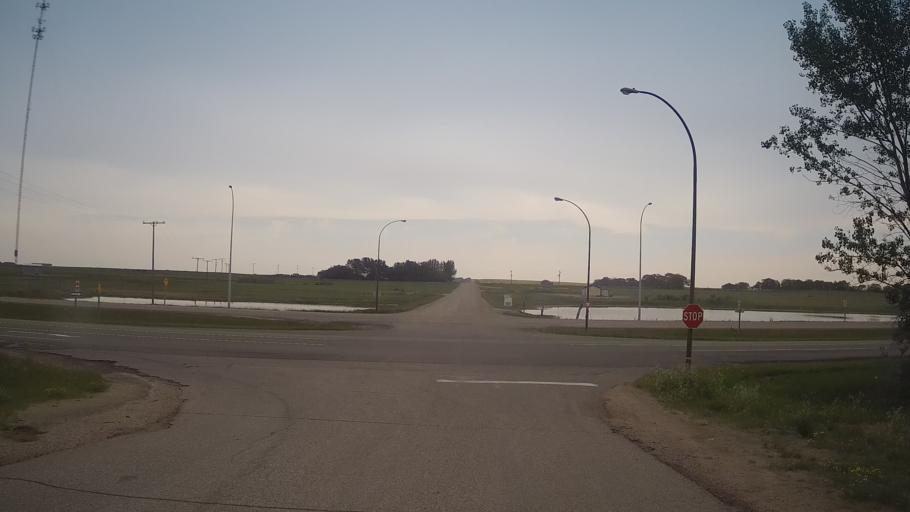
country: CA
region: Saskatchewan
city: Saskatoon
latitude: 51.8527
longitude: -106.5083
